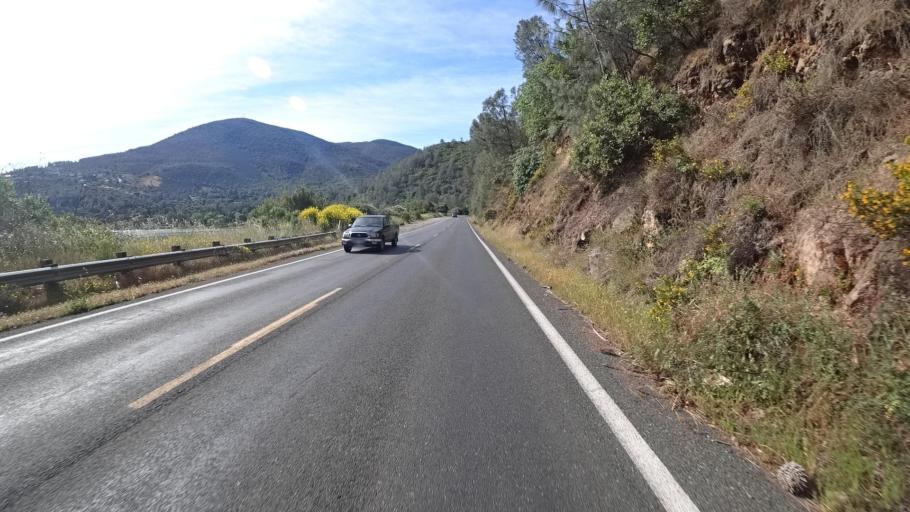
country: US
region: California
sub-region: Lake County
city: Soda Bay
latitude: 39.0061
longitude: -122.8003
